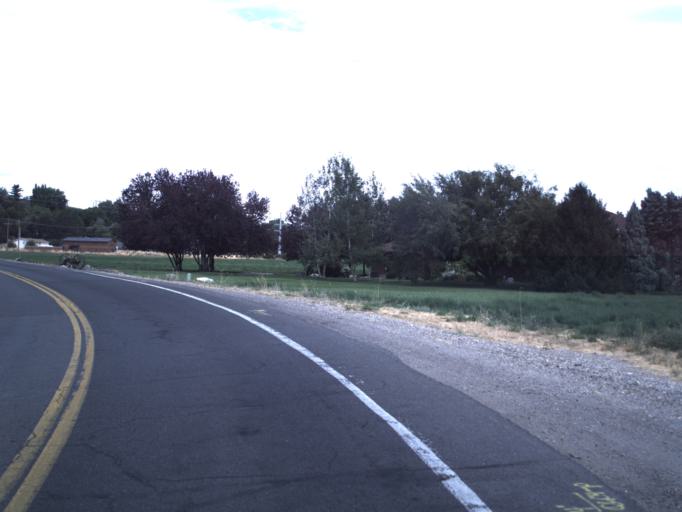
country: US
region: Utah
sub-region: Weber County
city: Riverdale
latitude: 41.1569
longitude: -111.9986
